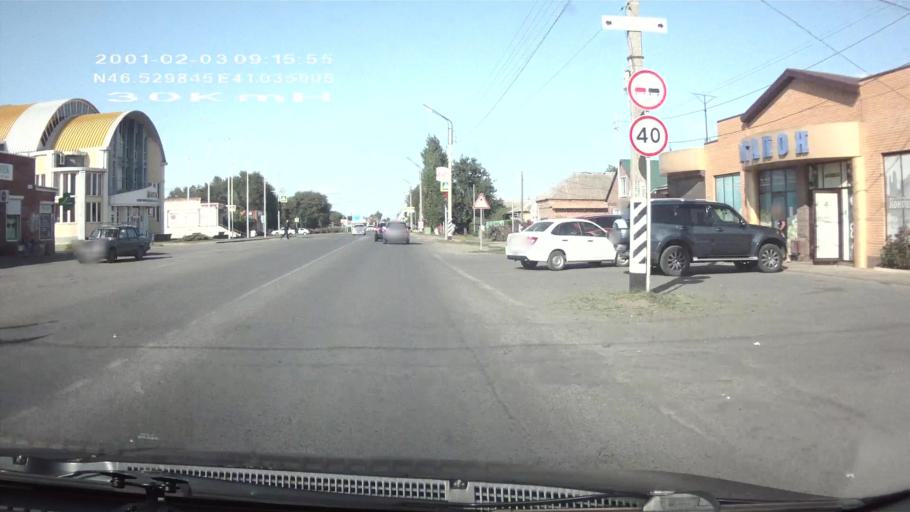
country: RU
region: Rostov
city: Tselina
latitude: 46.5298
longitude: 41.0356
